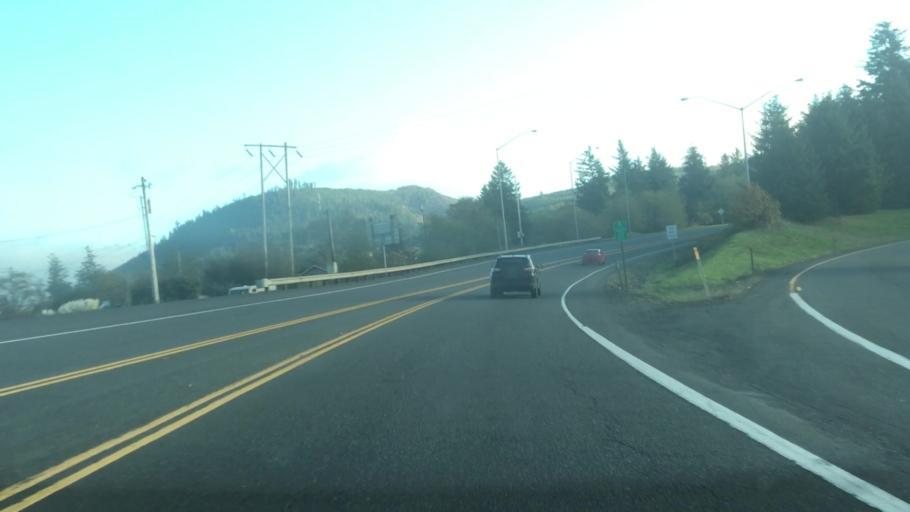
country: US
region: Oregon
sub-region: Clatsop County
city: Seaside
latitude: 45.9414
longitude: -123.9192
